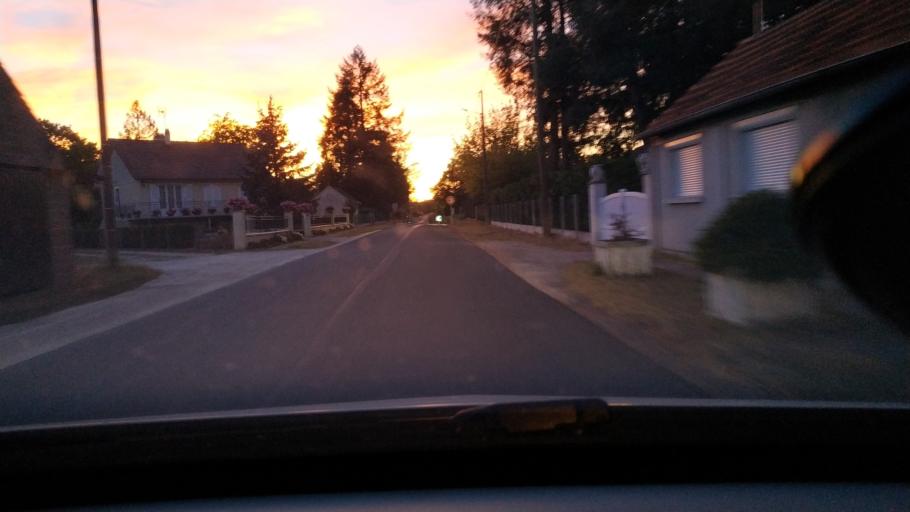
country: FR
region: Centre
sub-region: Departement du Cher
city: Brinon-sur-Sauldre
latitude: 47.6089
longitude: 2.1717
